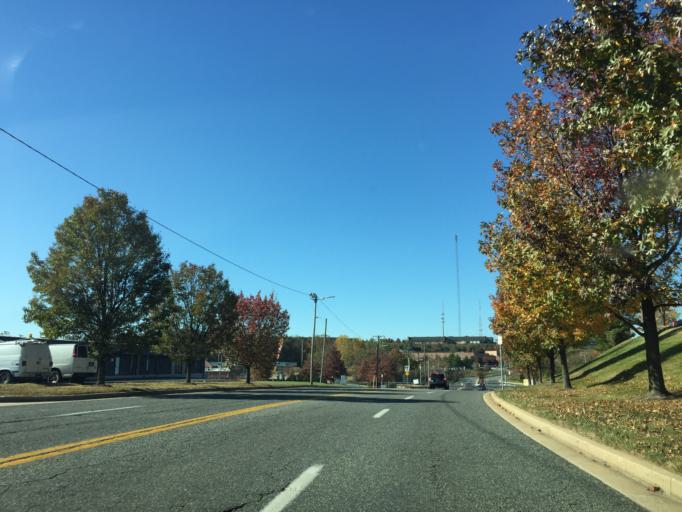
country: US
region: Maryland
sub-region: Baltimore County
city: Lansdowne
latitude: 39.2525
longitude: -76.6660
